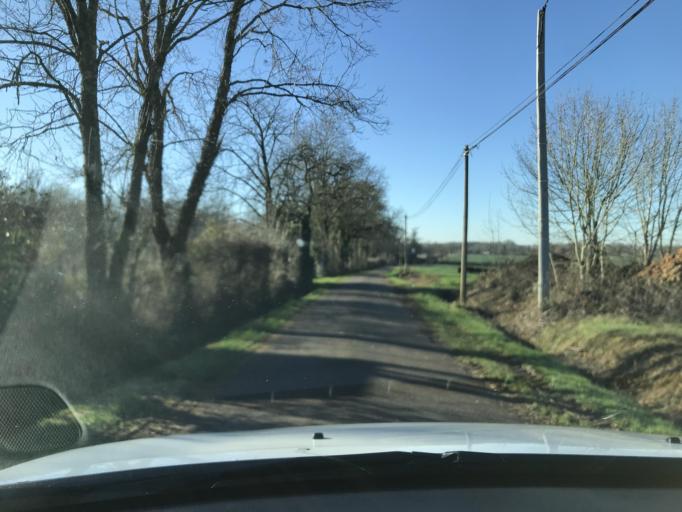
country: FR
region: Poitou-Charentes
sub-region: Departement de la Charente
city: Loubert
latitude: 45.8460
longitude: 0.5435
